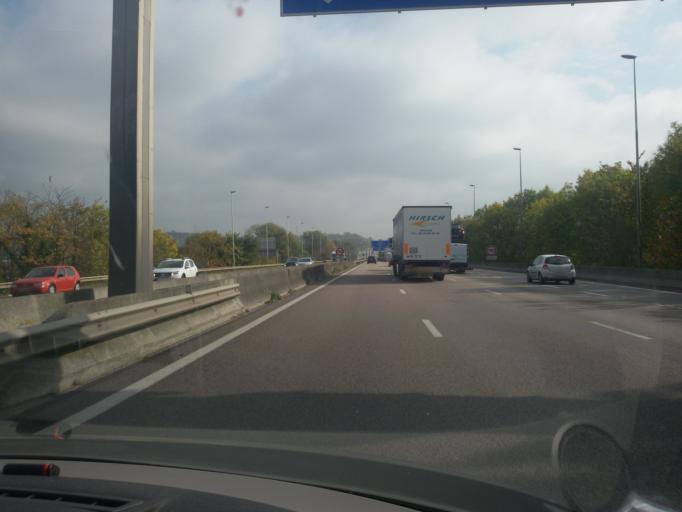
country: FR
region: Haute-Normandie
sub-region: Departement de la Seine-Maritime
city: Oissel
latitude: 49.3315
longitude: 1.0835
